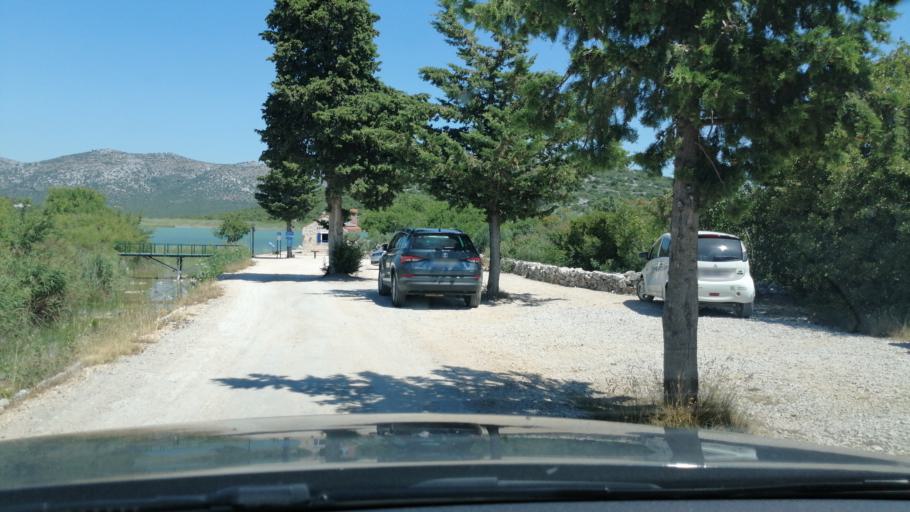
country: HR
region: Sibensko-Kniniska
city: Murter
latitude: 43.8493
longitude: 15.6288
